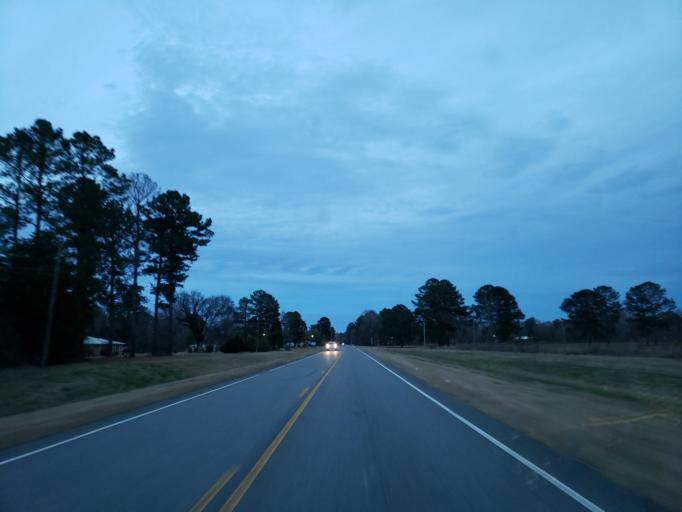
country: US
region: Alabama
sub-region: Greene County
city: Eutaw
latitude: 32.8474
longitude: -88.1202
